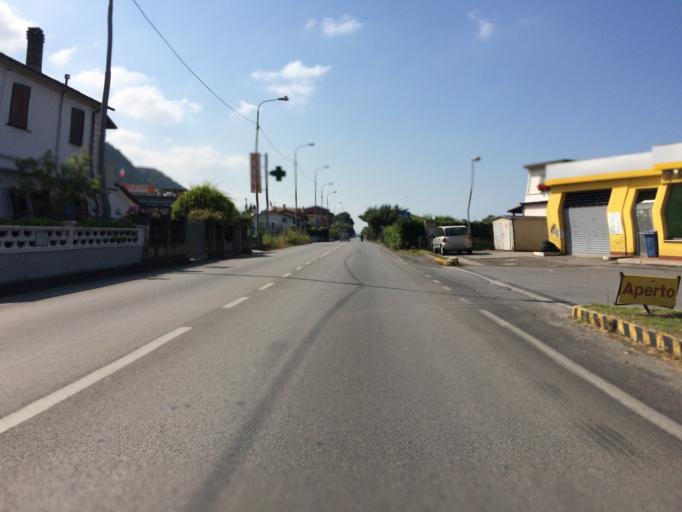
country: IT
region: Tuscany
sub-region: Provincia di Massa-Carrara
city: San Vito-Cerreto
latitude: 44.0155
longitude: 10.1565
